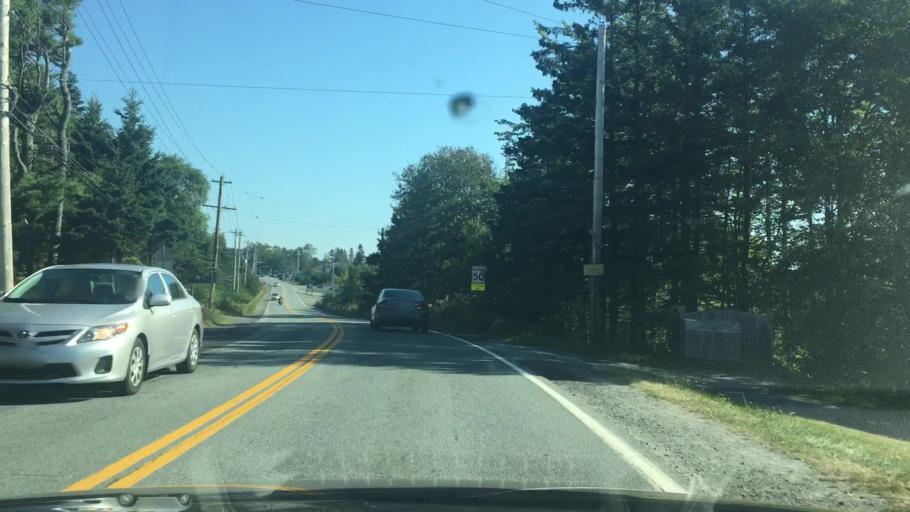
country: CA
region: Nova Scotia
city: Cole Harbour
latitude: 44.7837
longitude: -63.1524
